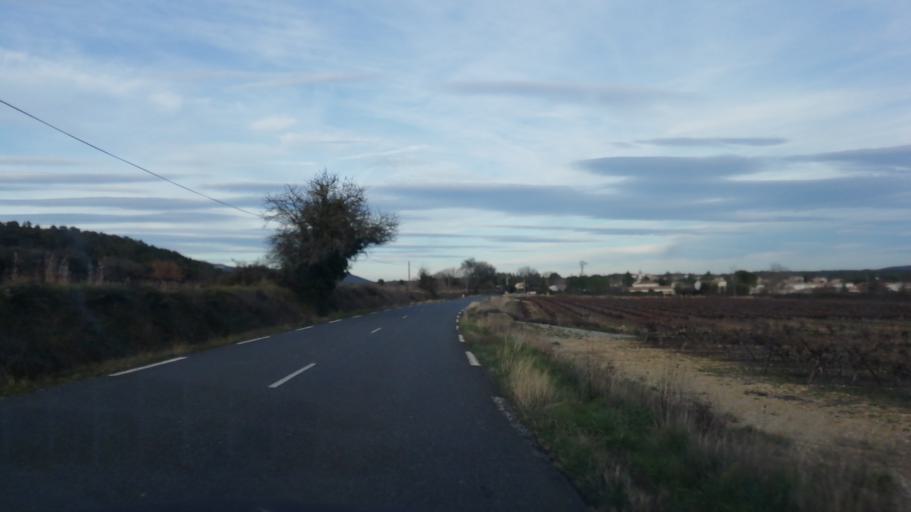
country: FR
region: Languedoc-Roussillon
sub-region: Departement de l'Herault
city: Claret
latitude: 43.8395
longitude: 3.9350
